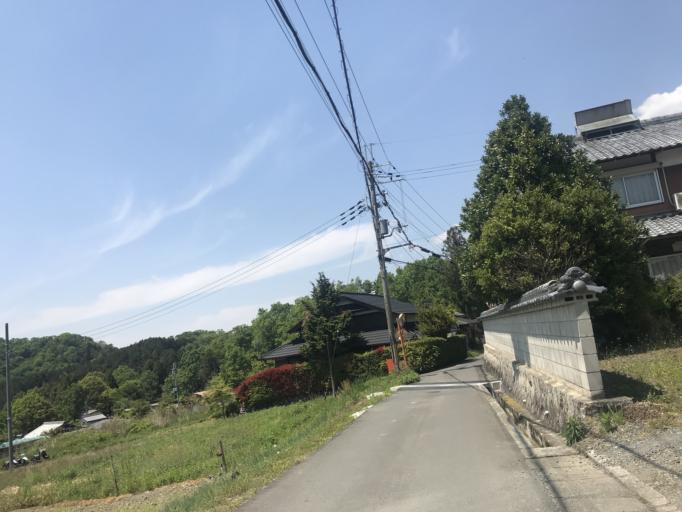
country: JP
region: Kyoto
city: Kameoka
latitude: 35.0679
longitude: 135.5707
